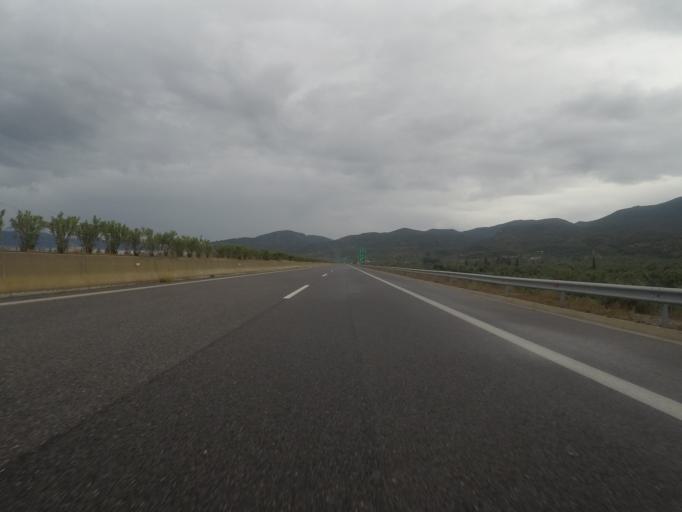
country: GR
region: Peloponnese
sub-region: Nomos Messinias
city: Meligalas
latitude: 37.2389
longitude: 22.0173
